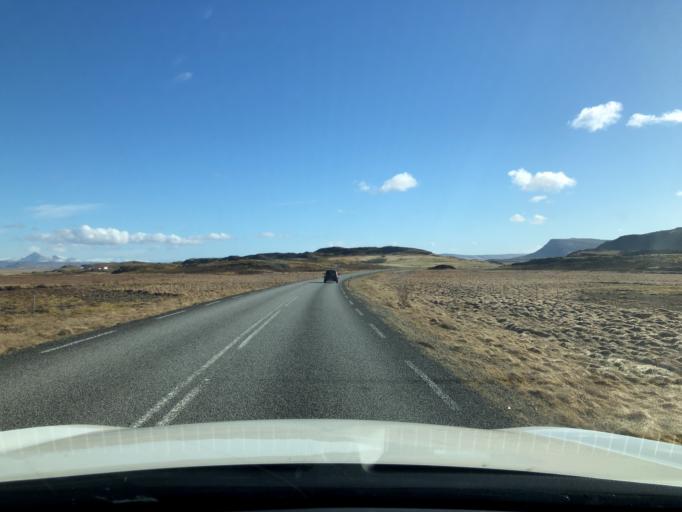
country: IS
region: West
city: Borgarnes
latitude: 64.5680
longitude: -21.6858
